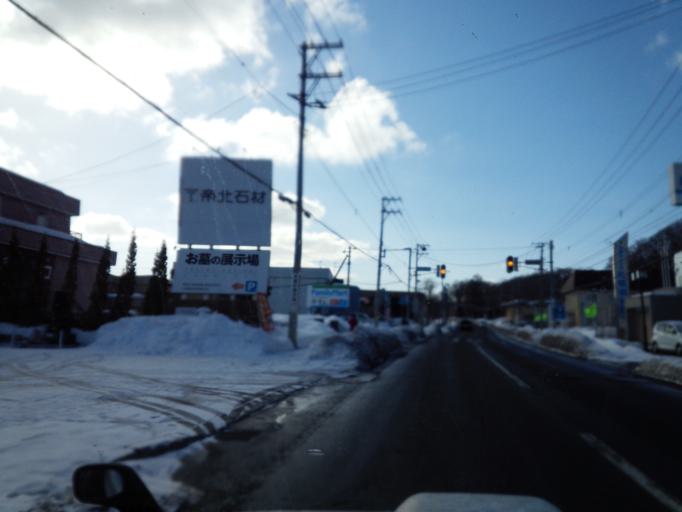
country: JP
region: Hokkaido
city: Sapporo
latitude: 42.9548
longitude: 141.3445
